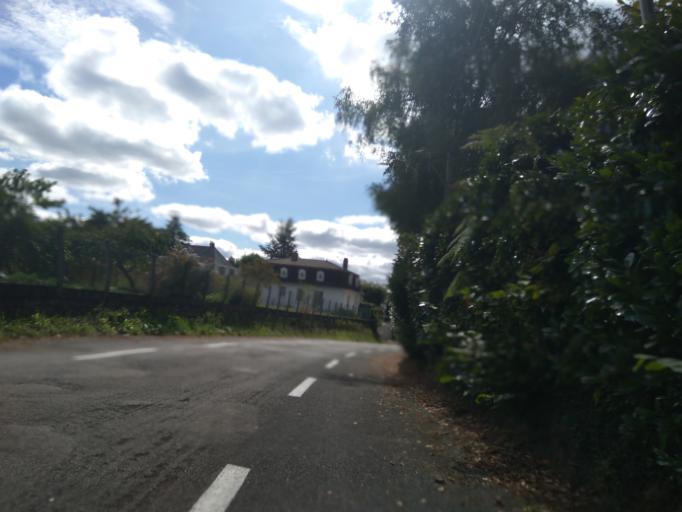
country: FR
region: Aquitaine
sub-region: Departement des Pyrenees-Atlantiques
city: Idron
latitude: 43.2981
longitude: -0.3276
